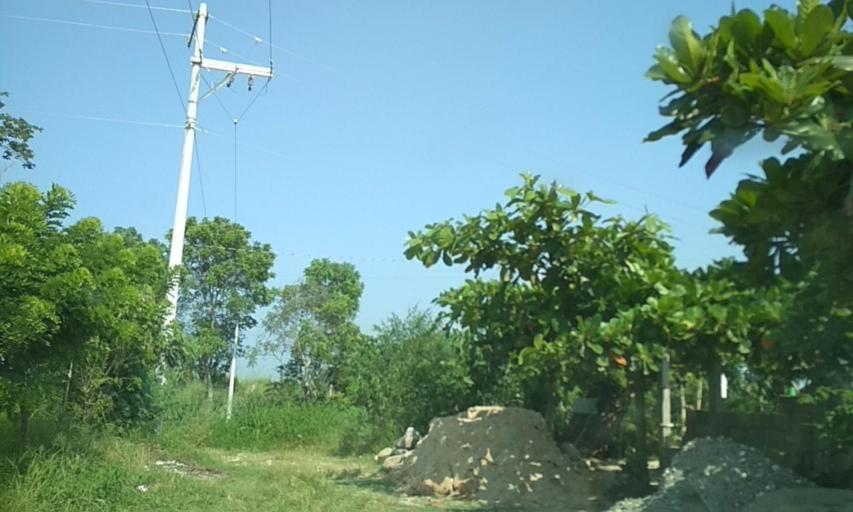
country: MX
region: Veracruz
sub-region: Atzalan
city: Colonias Pedernales
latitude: 20.0530
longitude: -96.9932
